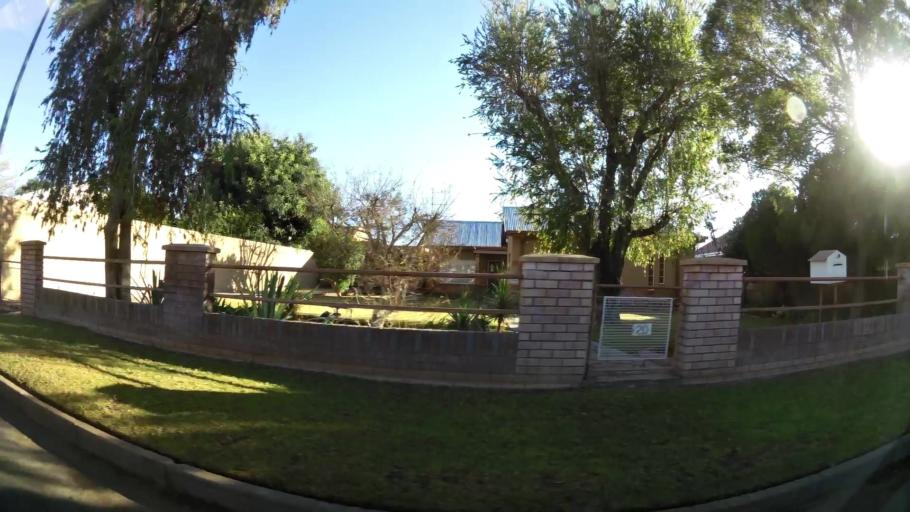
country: ZA
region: Northern Cape
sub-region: Frances Baard District Municipality
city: Kimberley
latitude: -28.7418
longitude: 24.7317
